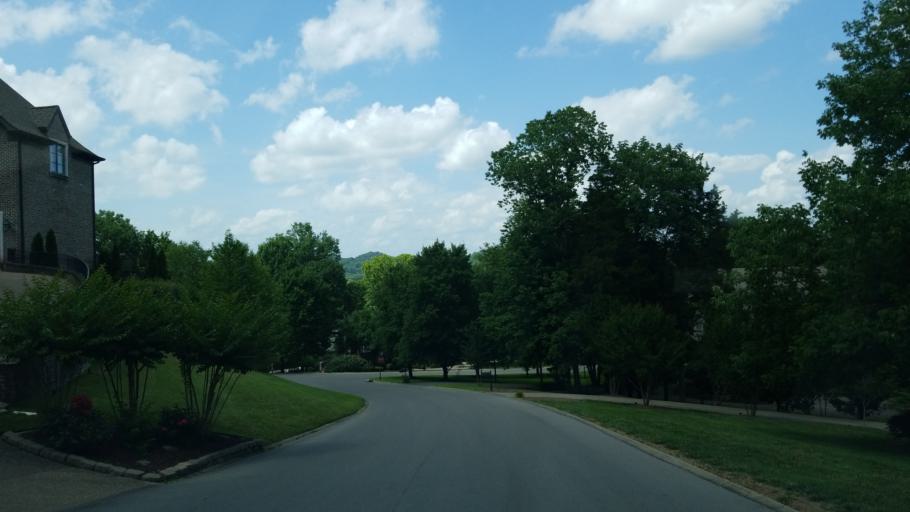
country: US
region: Tennessee
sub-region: Davidson County
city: Forest Hills
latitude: 36.0392
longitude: -86.8644
